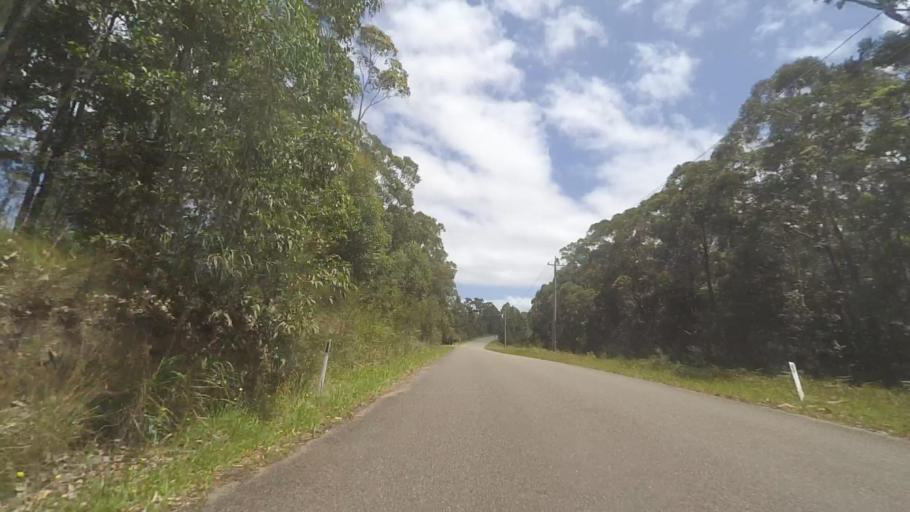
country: AU
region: New South Wales
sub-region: Shoalhaven Shire
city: Milton
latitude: -35.4089
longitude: 150.3564
